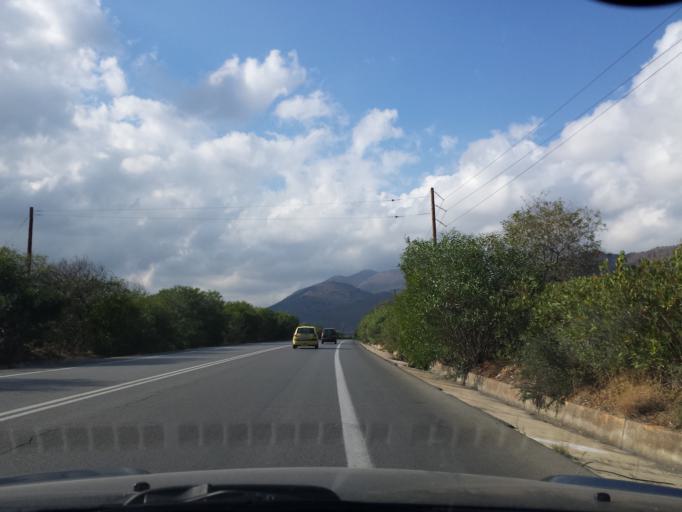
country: GR
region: Crete
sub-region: Nomos Lasithiou
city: Neapoli
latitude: 35.2321
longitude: 25.6522
